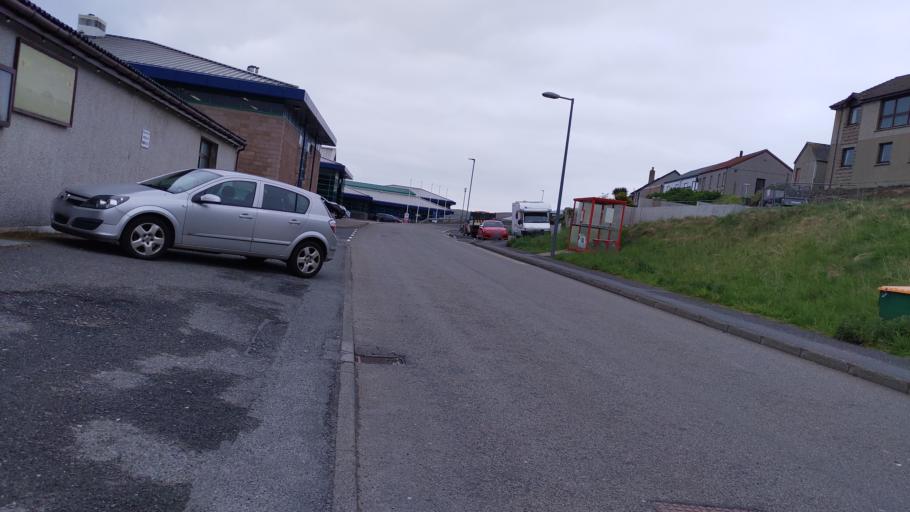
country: GB
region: Scotland
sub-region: Shetland Islands
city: Lerwick
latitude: 60.1339
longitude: -1.2860
